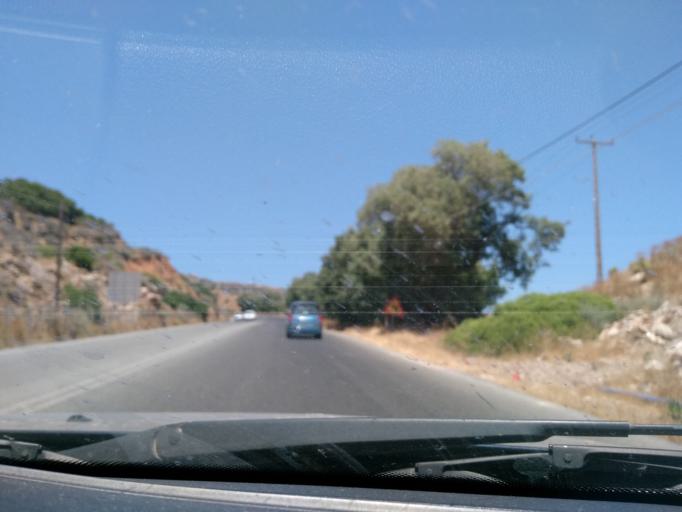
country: GR
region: Crete
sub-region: Nomos Irakleiou
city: Gazi
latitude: 35.3687
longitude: 25.0382
